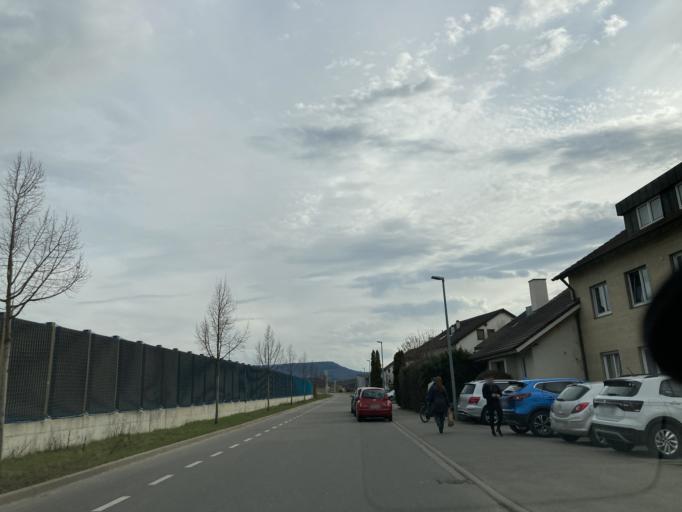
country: DE
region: Baden-Wuerttemberg
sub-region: Tuebingen Region
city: Dusslingen
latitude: 48.4470
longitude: 9.0579
